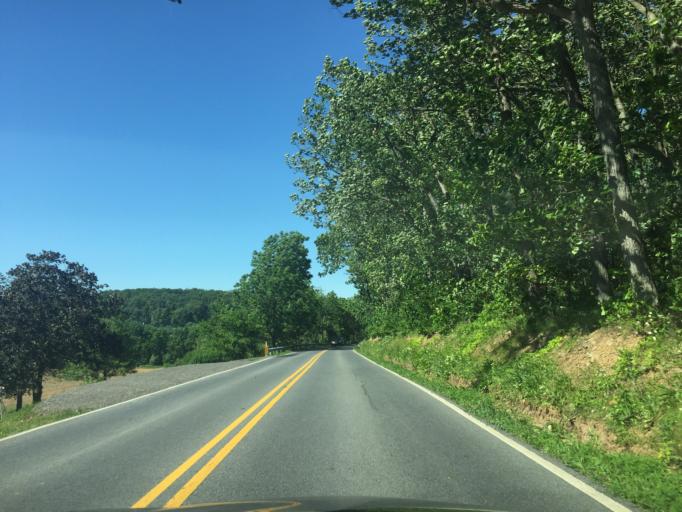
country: US
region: Maryland
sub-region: Carroll County
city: Westminster
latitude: 39.5913
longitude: -76.9253
